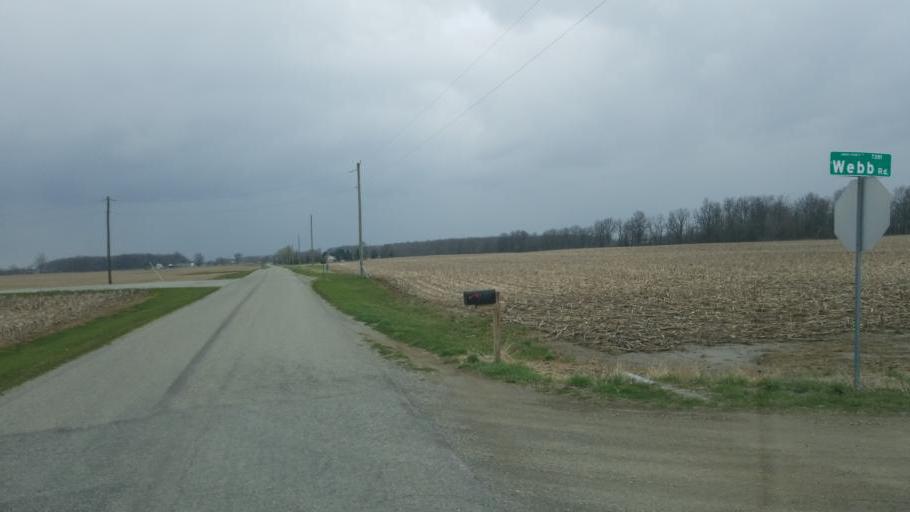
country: US
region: Ohio
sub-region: Union County
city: Richwood
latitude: 40.4164
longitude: -83.3879
